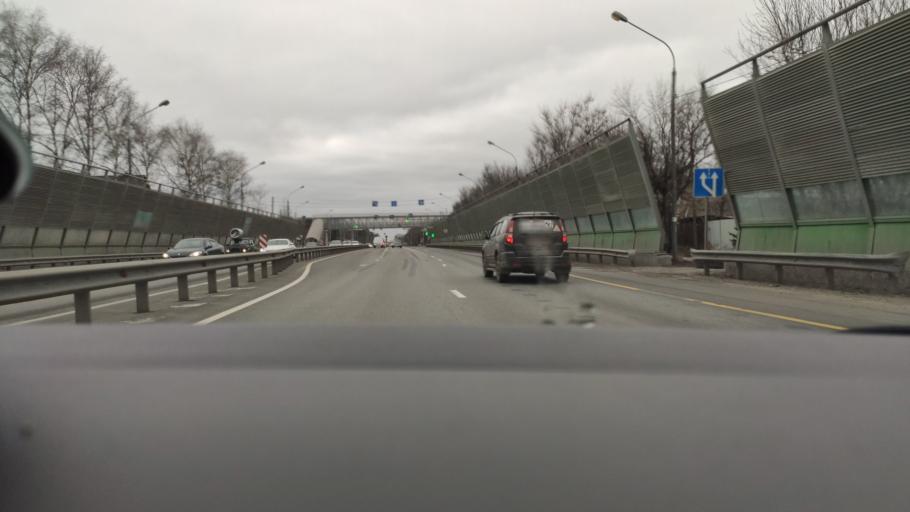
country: RU
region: Moskovskaya
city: Vishnyakovskiye Dachi
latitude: 55.8141
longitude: 38.1133
